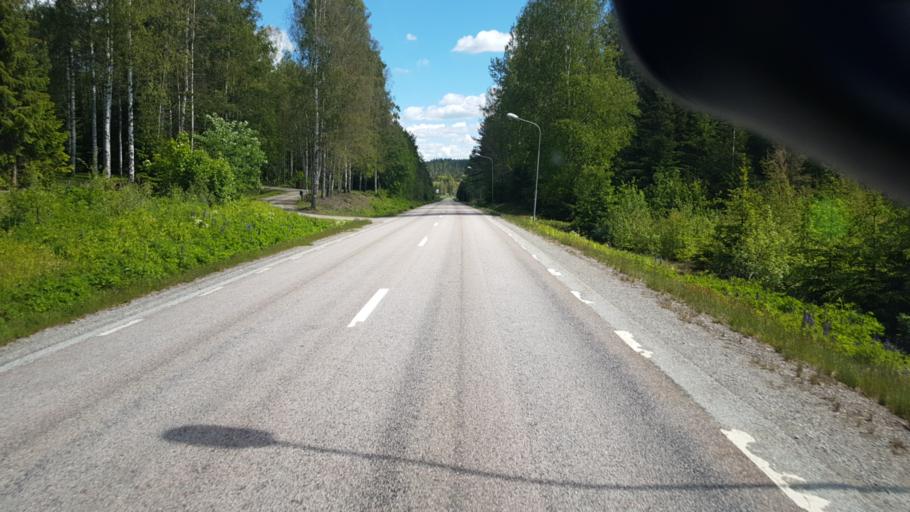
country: SE
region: Vaermland
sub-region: Arvika Kommun
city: Arvika
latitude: 59.6467
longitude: 12.7603
